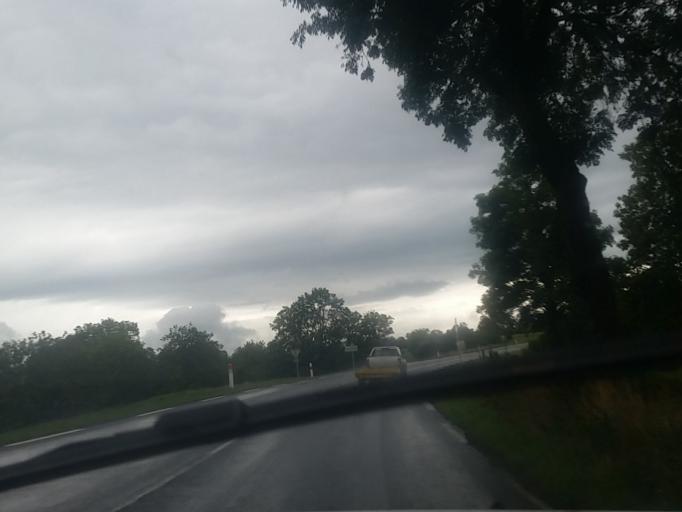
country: FR
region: Auvergne
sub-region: Departement du Cantal
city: Murat
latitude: 45.0844
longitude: 2.9267
